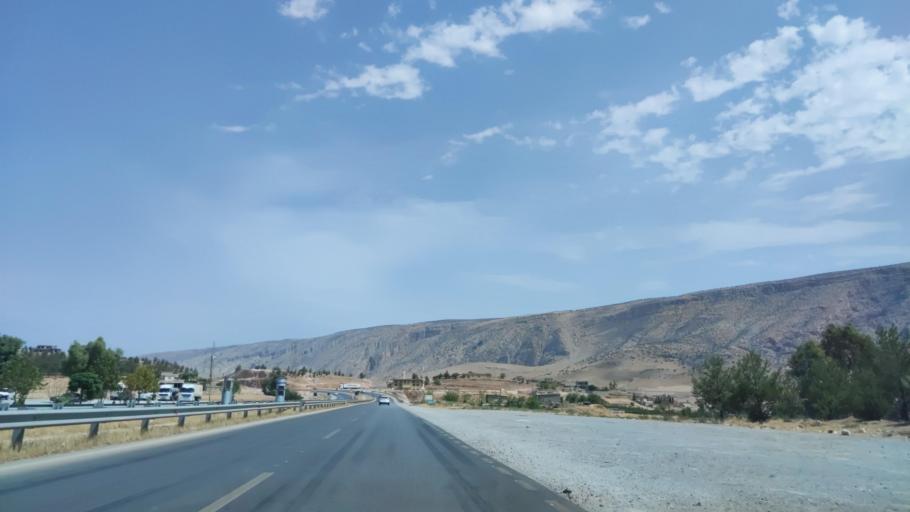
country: IQ
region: Arbil
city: Shaqlawah
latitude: 36.4821
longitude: 44.3810
